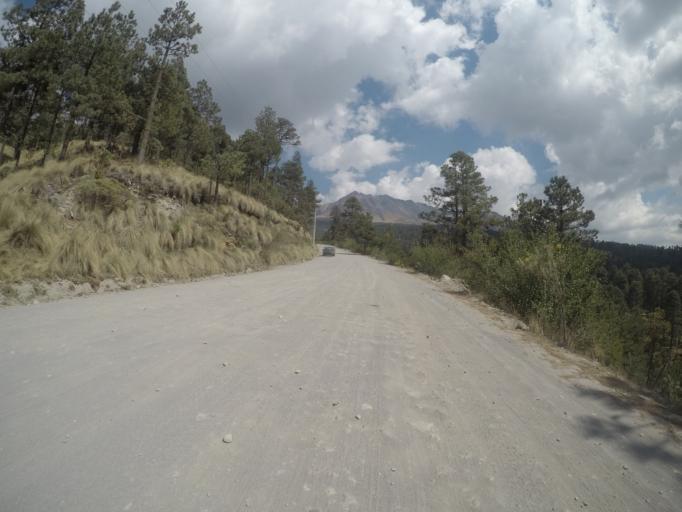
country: MX
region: Mexico
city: Cerro La Calera
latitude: 19.1353
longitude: -99.7975
